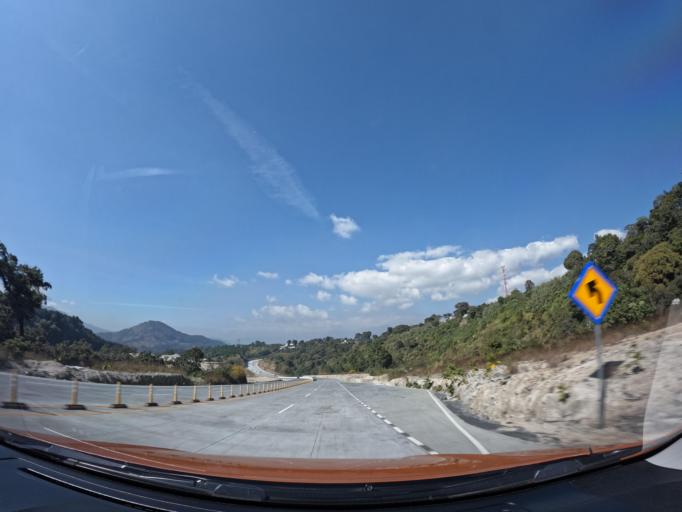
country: GT
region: Guatemala
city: Villa Canales
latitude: 14.4939
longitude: -90.5206
